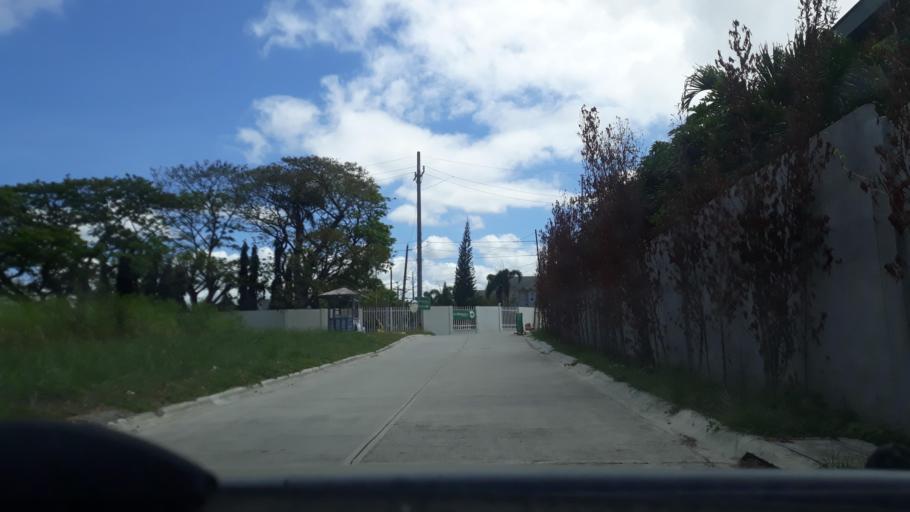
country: PH
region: Calabarzon
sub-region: Province of Cavite
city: Dasmarinas
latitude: 14.3189
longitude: 120.9461
